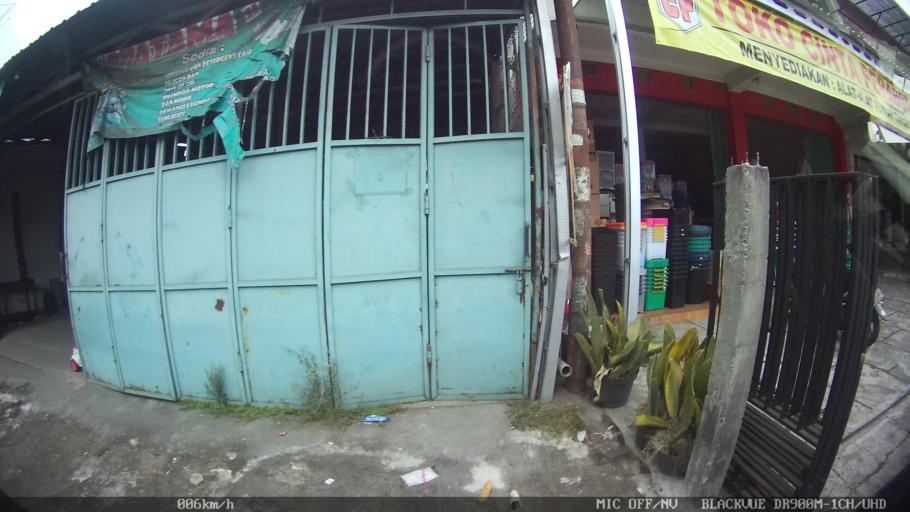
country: ID
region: Daerah Istimewa Yogyakarta
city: Depok
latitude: -7.8028
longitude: 110.4145
